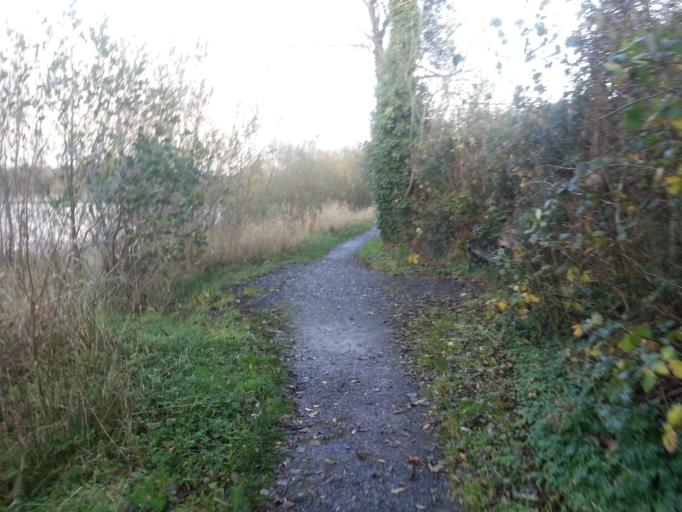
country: IE
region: Ulster
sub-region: County Monaghan
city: Clones
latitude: 54.2265
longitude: -7.2811
